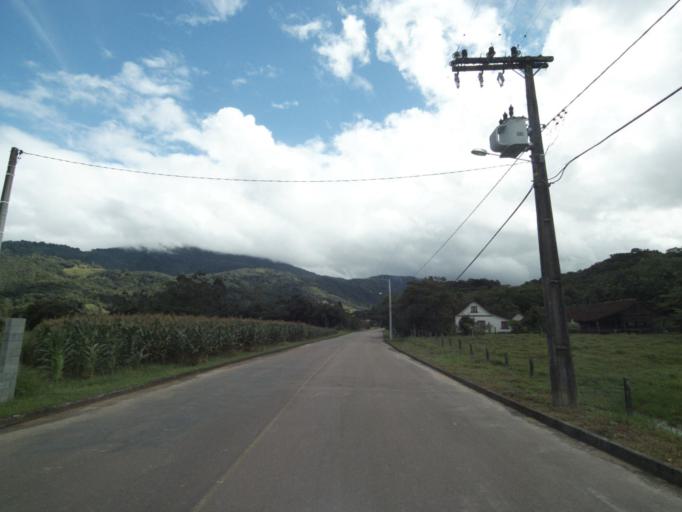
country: BR
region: Santa Catarina
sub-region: Pomerode
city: Pomerode
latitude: -26.6810
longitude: -49.1776
